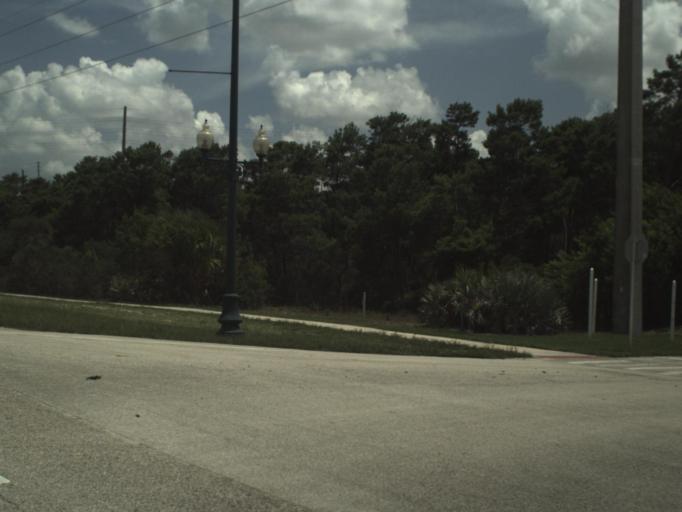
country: US
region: Florida
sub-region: Martin County
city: Hobe Sound
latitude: 27.0544
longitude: -80.1339
